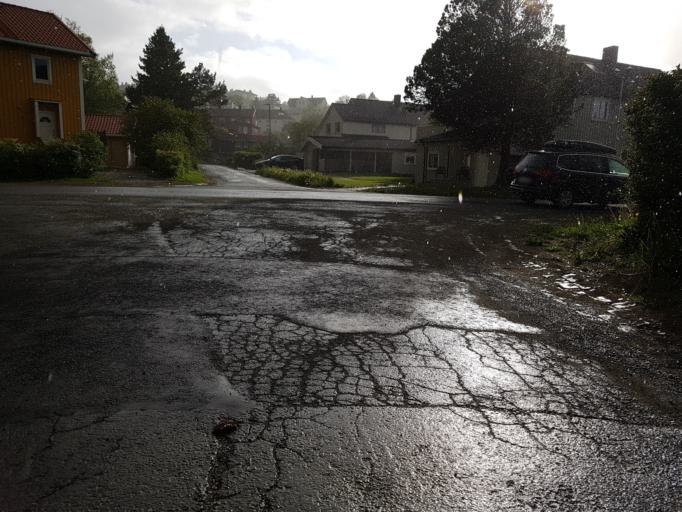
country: NO
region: Sor-Trondelag
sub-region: Trondheim
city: Trondheim
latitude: 63.4334
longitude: 10.4411
